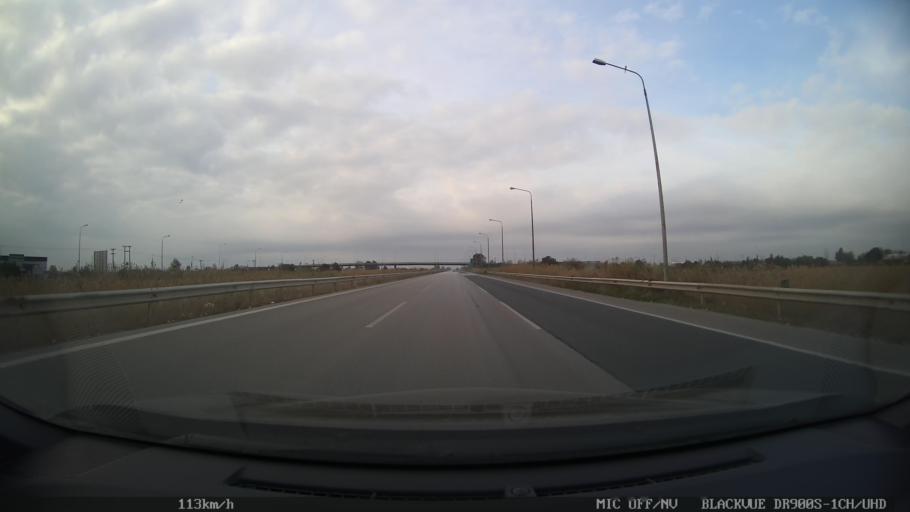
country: GR
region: Central Macedonia
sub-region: Nomos Thessalonikis
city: Sindos
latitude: 40.6466
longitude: 22.8060
